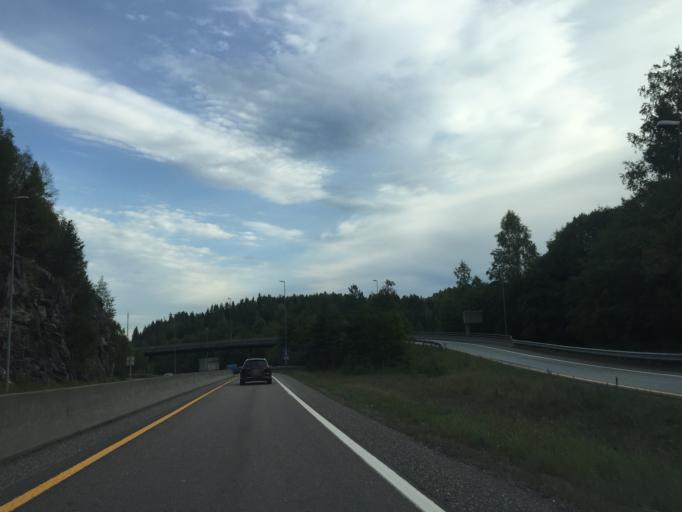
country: NO
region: Akershus
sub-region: Ski
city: Ski
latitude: 59.7387
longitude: 10.7825
